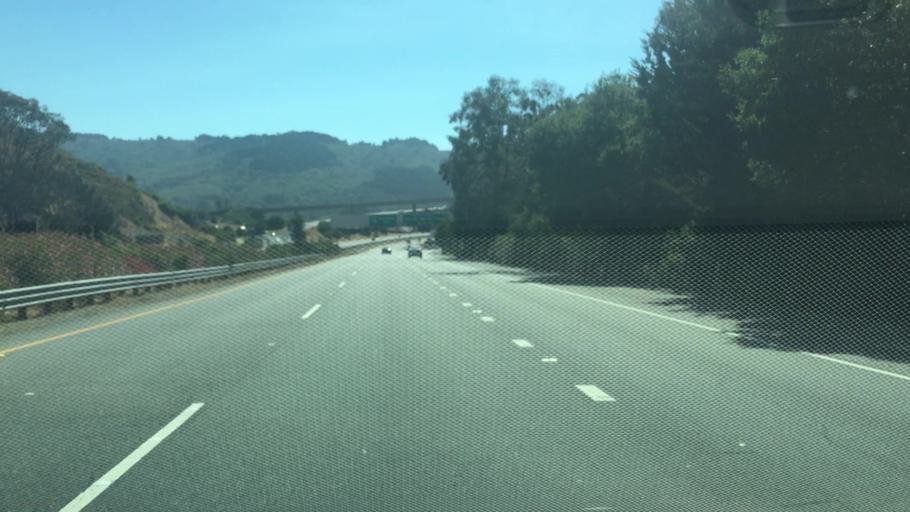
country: US
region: California
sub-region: San Mateo County
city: Highlands-Baywood Park
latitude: 37.5111
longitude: -122.3320
